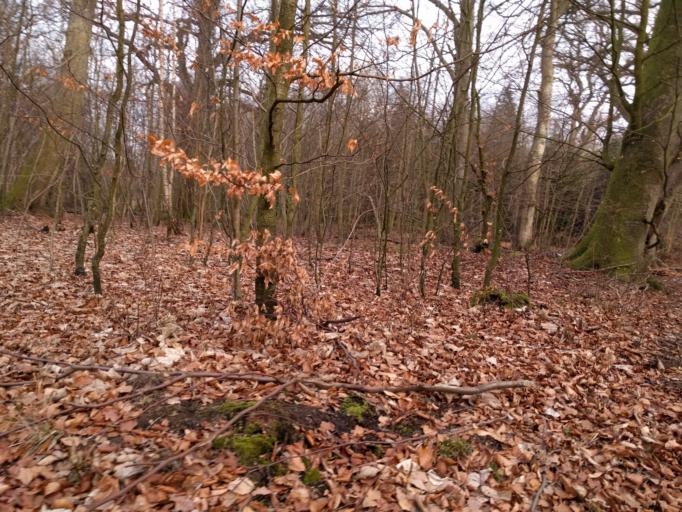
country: DK
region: Zealand
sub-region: Guldborgsund Kommune
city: Stubbekobing
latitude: 54.7749
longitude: 12.0114
